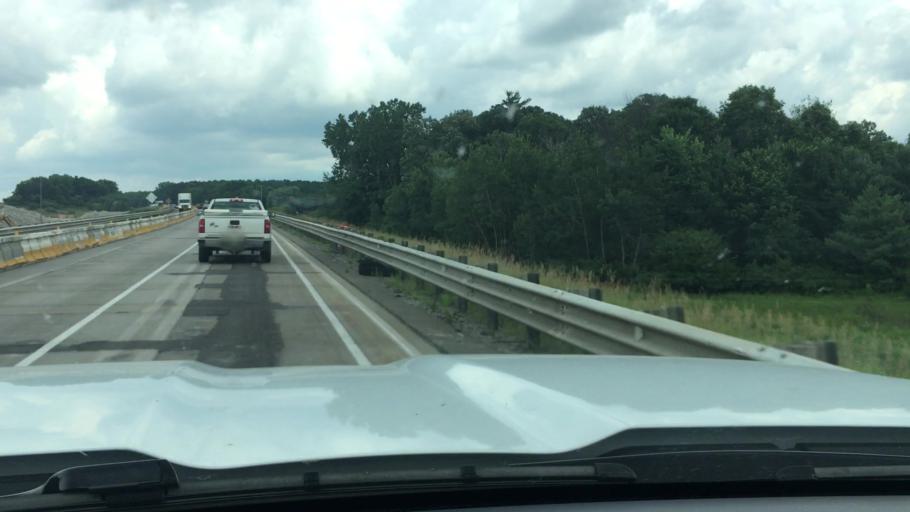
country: US
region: Michigan
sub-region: Kent County
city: Rockford
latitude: 43.1569
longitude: -85.5790
